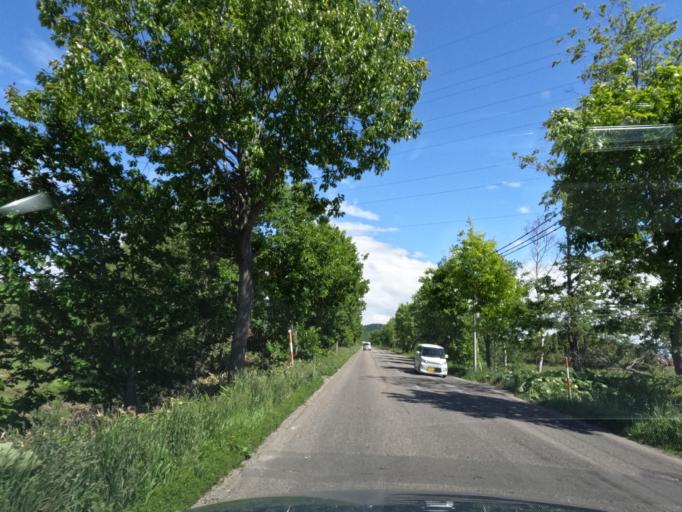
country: JP
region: Hokkaido
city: Kitahiroshima
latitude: 43.0193
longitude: 141.7146
